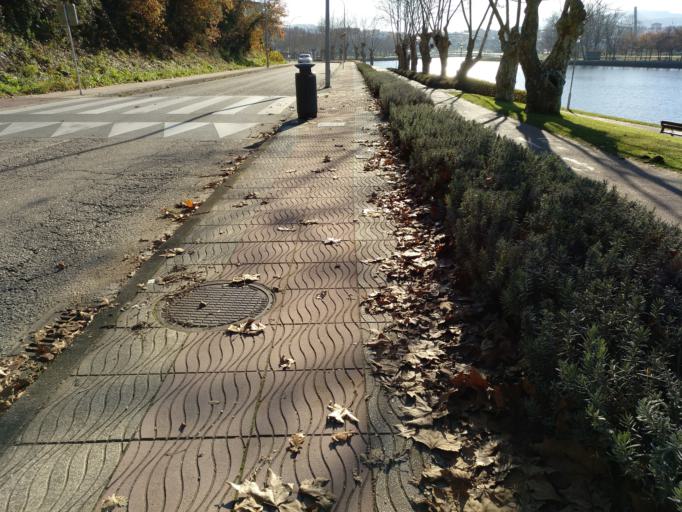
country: ES
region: Galicia
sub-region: Provincia de Pontevedra
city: Pontevedra
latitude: 42.4414
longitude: -8.6322
